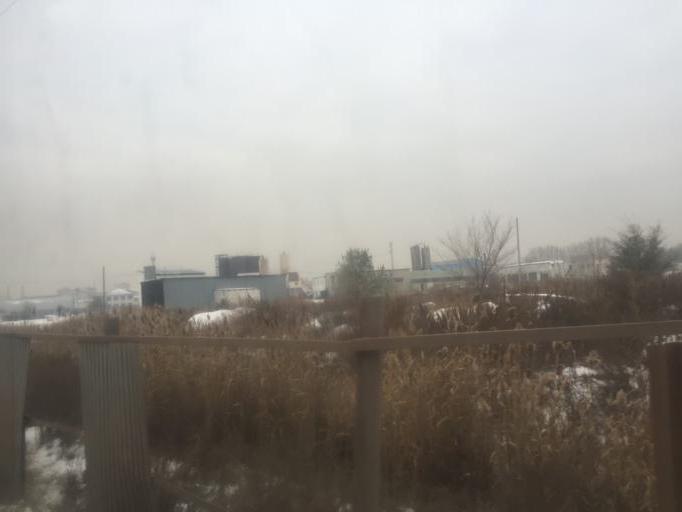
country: KZ
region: Astana Qalasy
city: Astana
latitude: 51.2005
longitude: 71.4105
